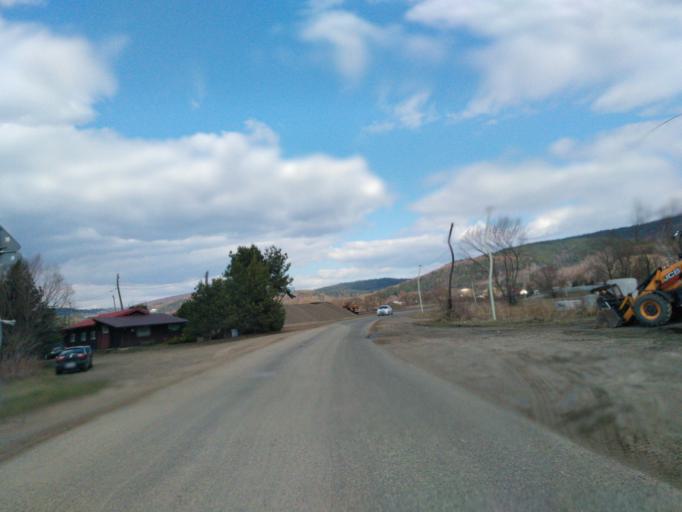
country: PL
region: Subcarpathian Voivodeship
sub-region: Powiat sanocki
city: Tyrawa Woloska
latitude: 49.6423
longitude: 22.2911
